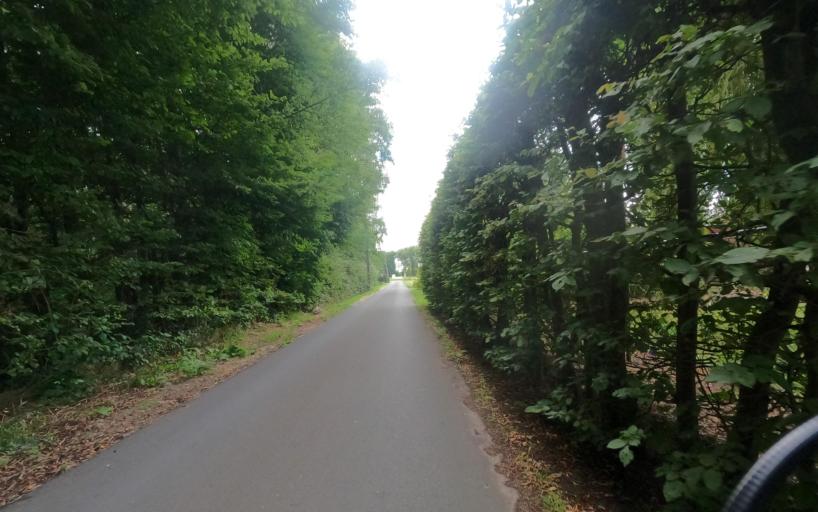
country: BE
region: Flanders
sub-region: Provincie Antwerpen
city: Putte
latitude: 51.0486
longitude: 4.6076
